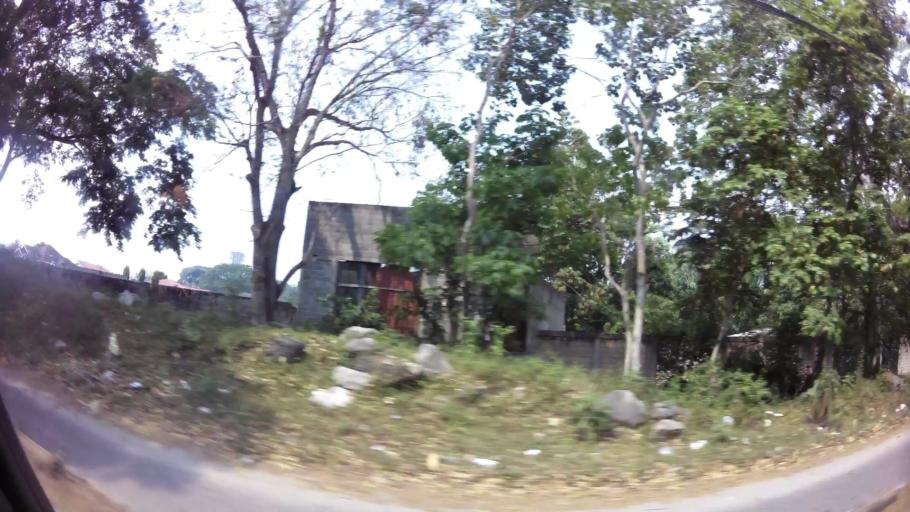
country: HN
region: Cortes
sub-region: San Pedro Sula
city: Pena Blanca
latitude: 15.5607
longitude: -88.0191
